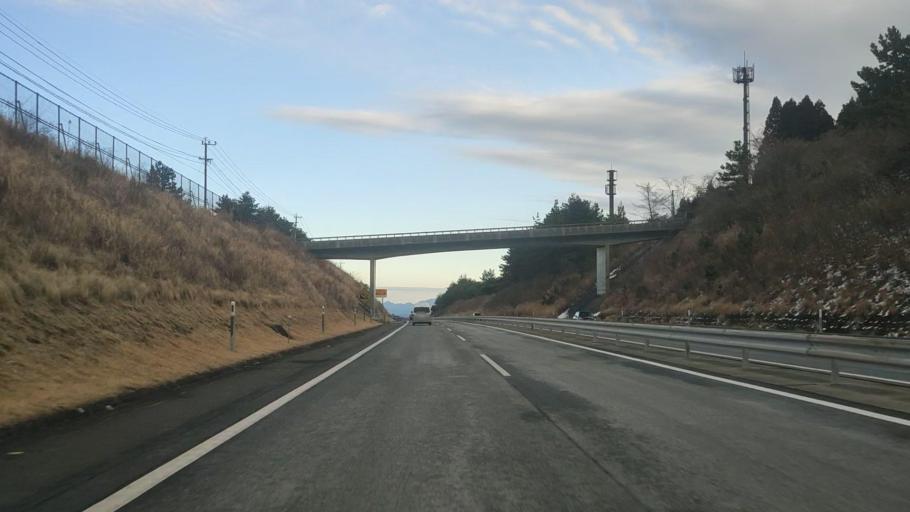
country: JP
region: Oita
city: Beppu
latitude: 33.3206
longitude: 131.4130
